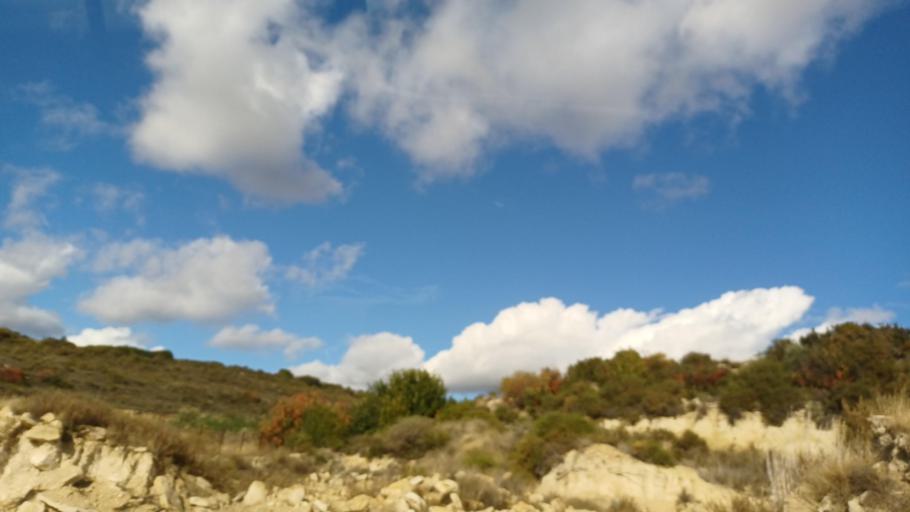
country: CY
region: Limassol
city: Sotira
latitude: 34.7475
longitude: 32.8593
